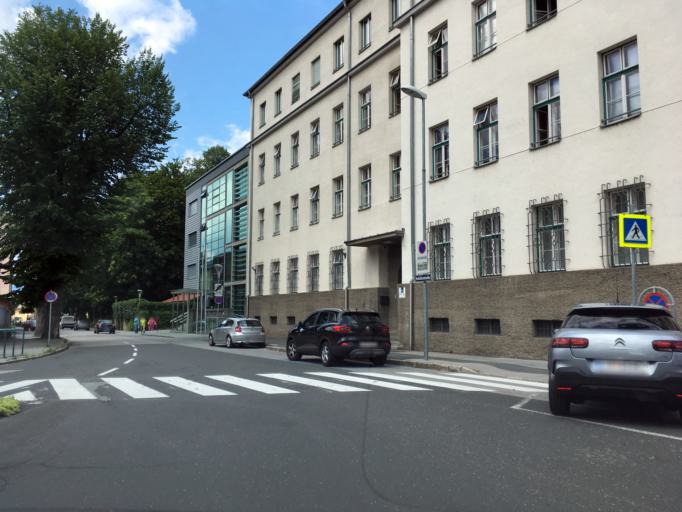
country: AT
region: Carinthia
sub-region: Politischer Bezirk Spittal an der Drau
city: Spittal an der Drau
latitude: 46.7967
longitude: 13.4950
